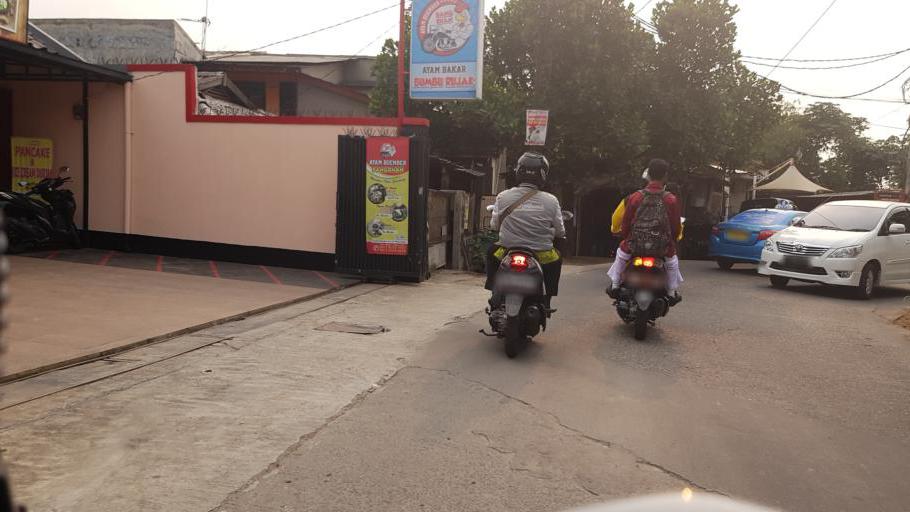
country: ID
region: West Java
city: Depok
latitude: -6.3727
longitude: 106.8429
